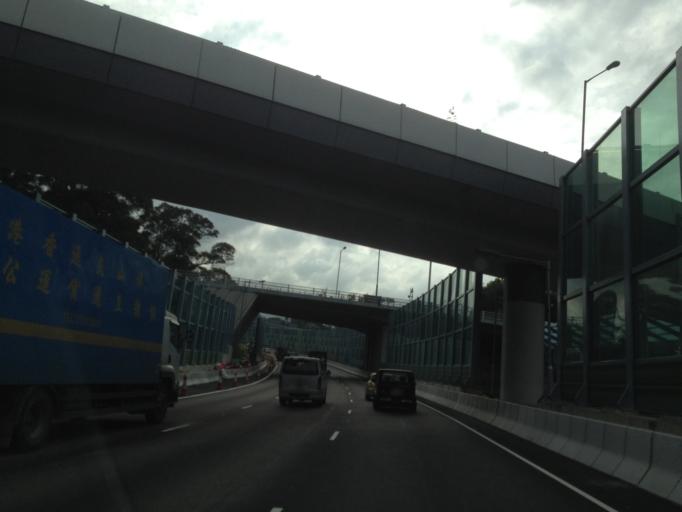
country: HK
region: Tai Po
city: Tai Po
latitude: 22.4447
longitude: 114.1774
